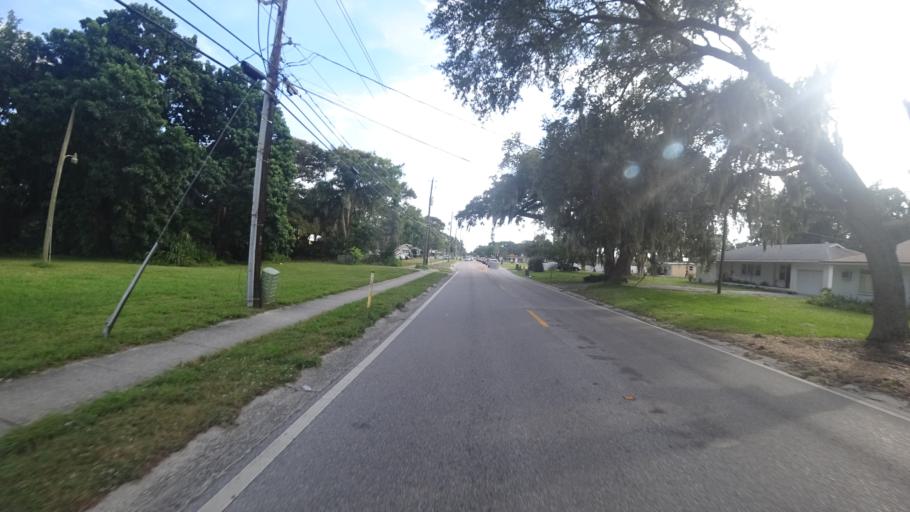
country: US
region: Florida
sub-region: Manatee County
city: West Samoset
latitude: 27.4600
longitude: -82.5671
